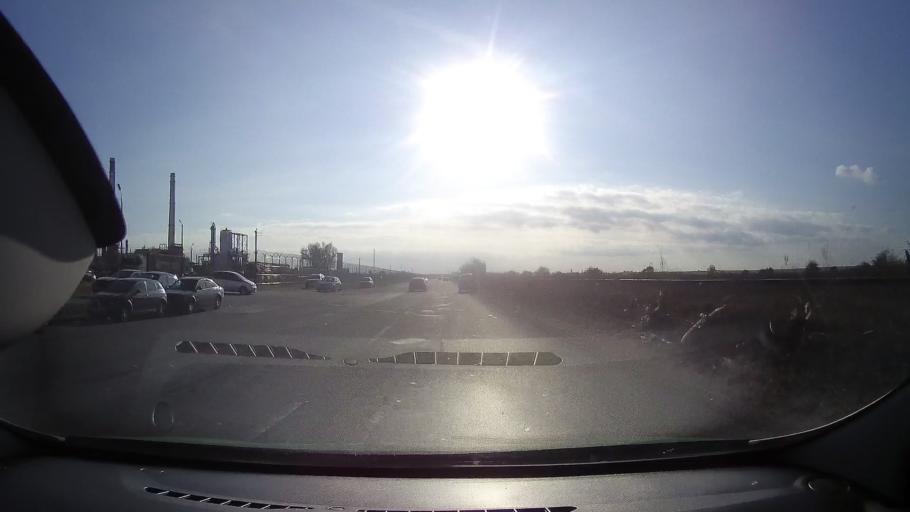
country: RO
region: Constanta
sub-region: Comuna Corbu
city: Corbu
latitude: 44.3441
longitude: 28.6417
